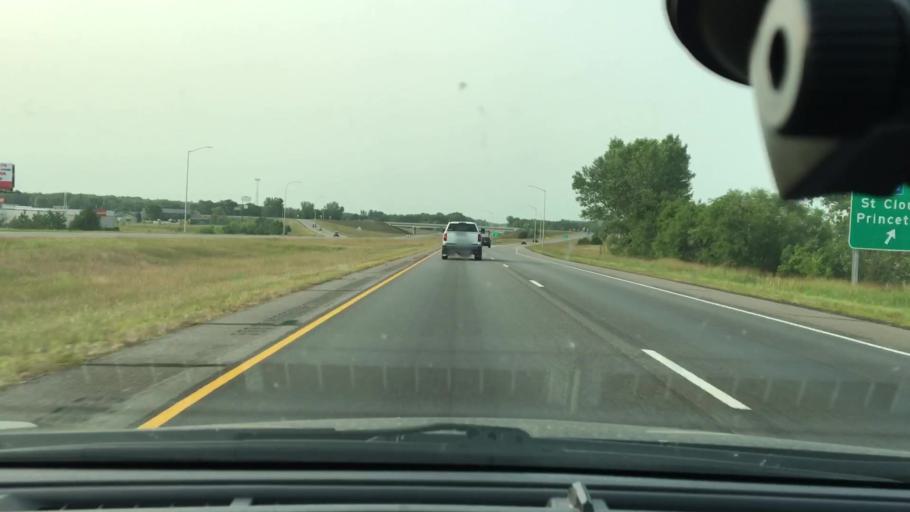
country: US
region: Minnesota
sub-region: Mille Lacs County
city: Princeton
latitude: 45.5715
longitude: -93.5983
